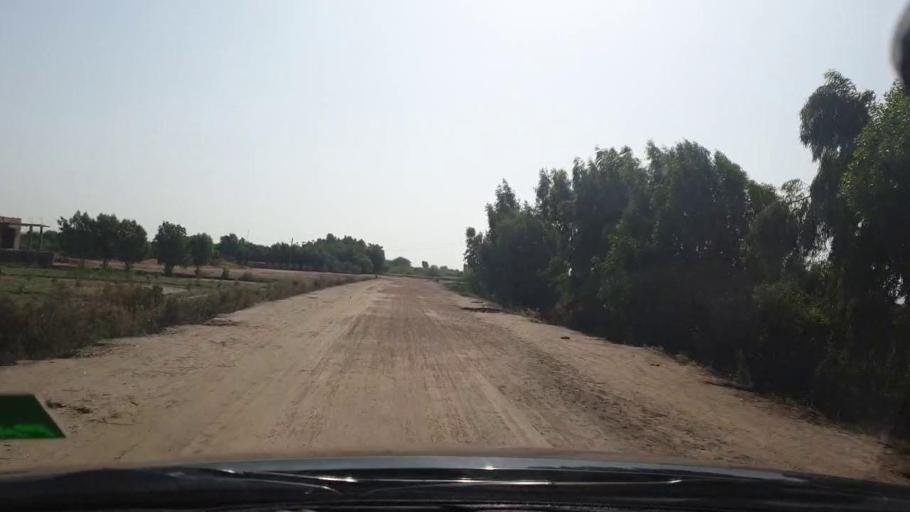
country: PK
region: Sindh
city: Tando Bago
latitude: 24.6974
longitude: 69.0171
